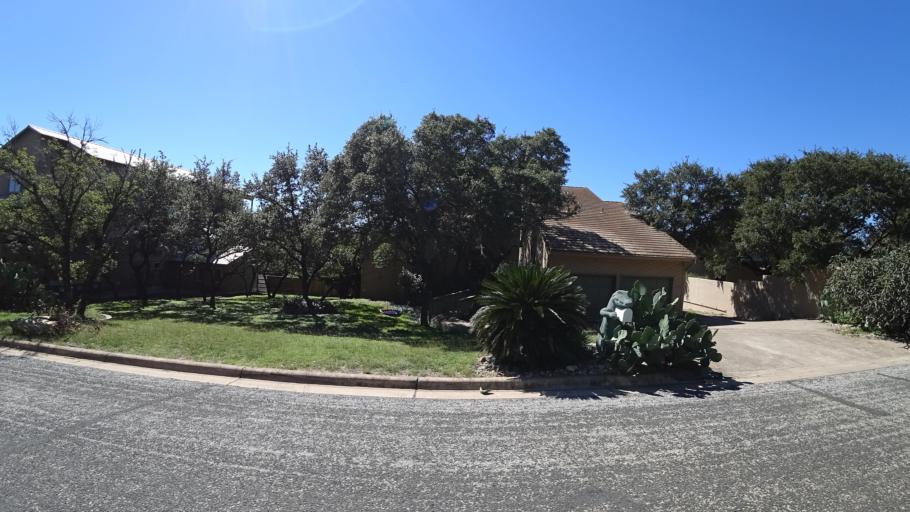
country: US
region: Texas
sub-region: Travis County
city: West Lake Hills
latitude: 30.3425
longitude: -97.7822
